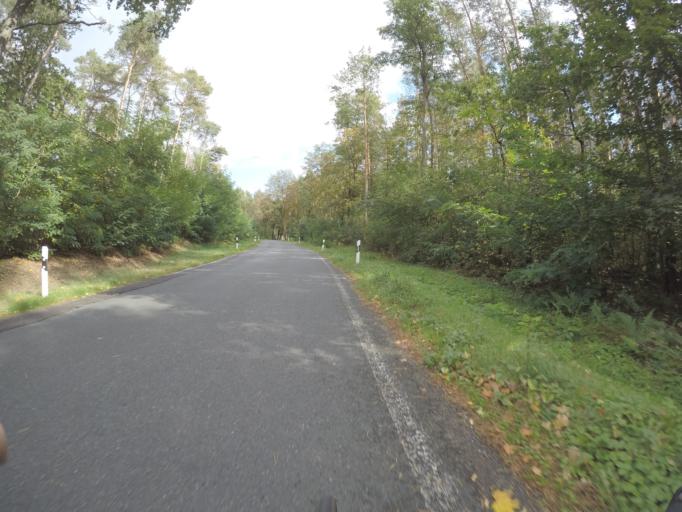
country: DE
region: Brandenburg
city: Strausberg
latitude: 52.6022
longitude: 13.8495
